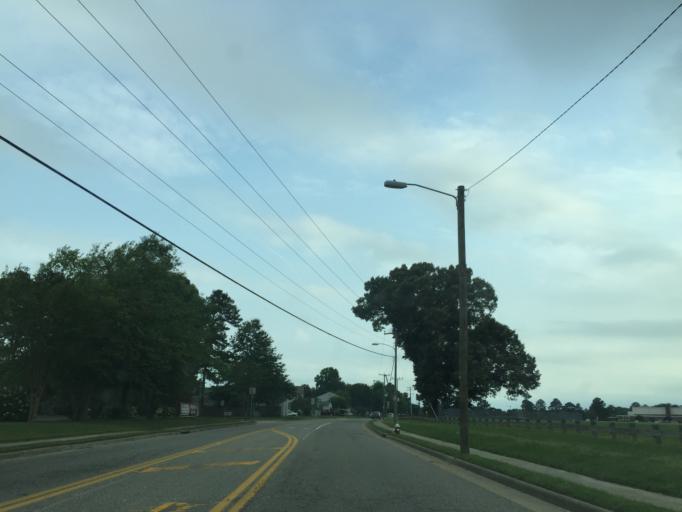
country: US
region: Virginia
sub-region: York County
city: Yorktown
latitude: 37.0995
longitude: -76.5266
